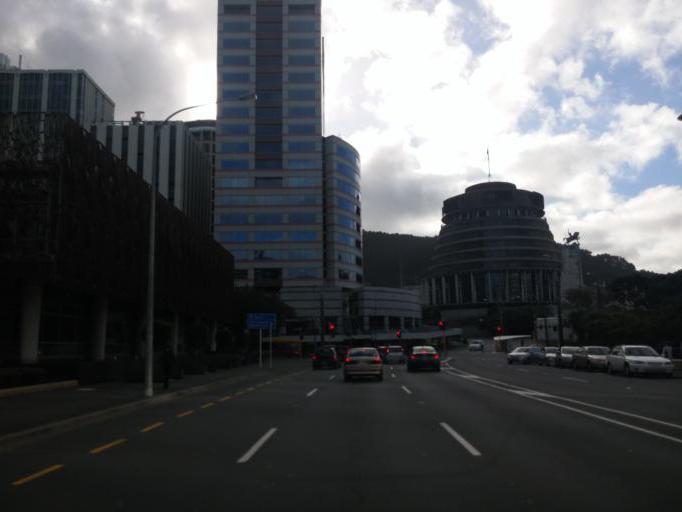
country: NZ
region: Wellington
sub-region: Wellington City
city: Wellington
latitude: -41.2802
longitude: 174.7775
